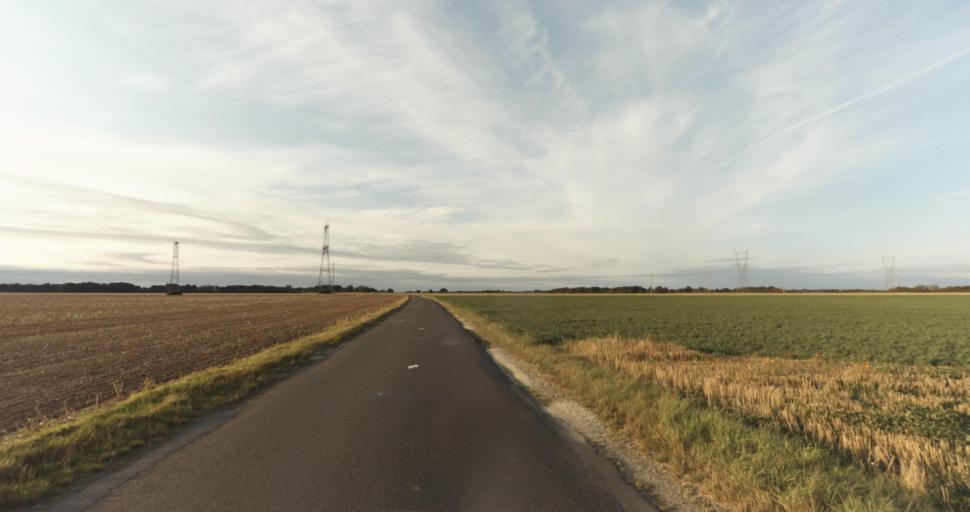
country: FR
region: Haute-Normandie
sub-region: Departement de l'Eure
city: Marcilly-sur-Eure
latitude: 48.8527
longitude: 1.2740
